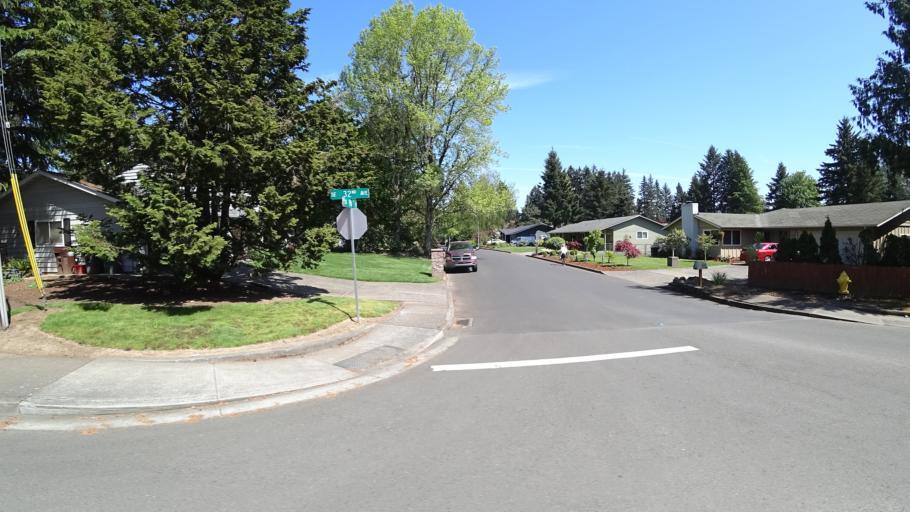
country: US
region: Oregon
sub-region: Washington County
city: Hillsboro
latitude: 45.5114
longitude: -122.9496
